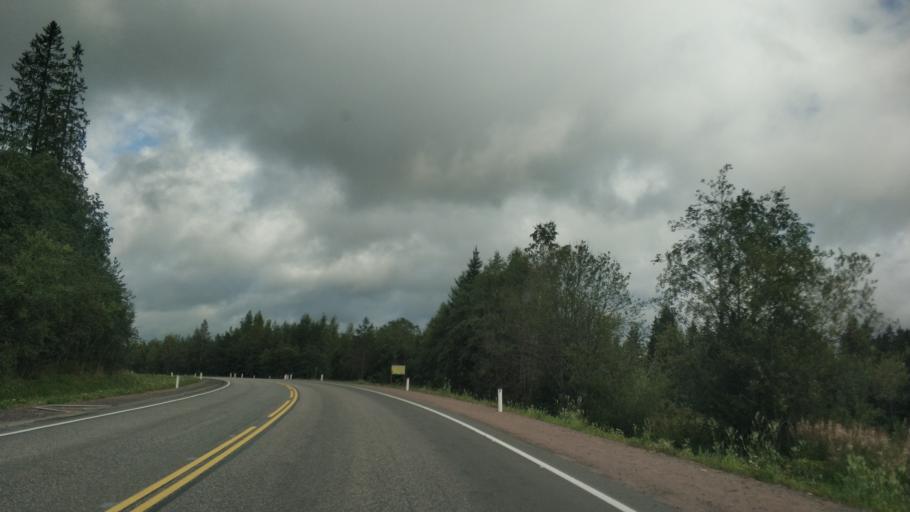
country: RU
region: Republic of Karelia
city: Khelyulya
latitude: 61.7842
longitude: 30.6544
